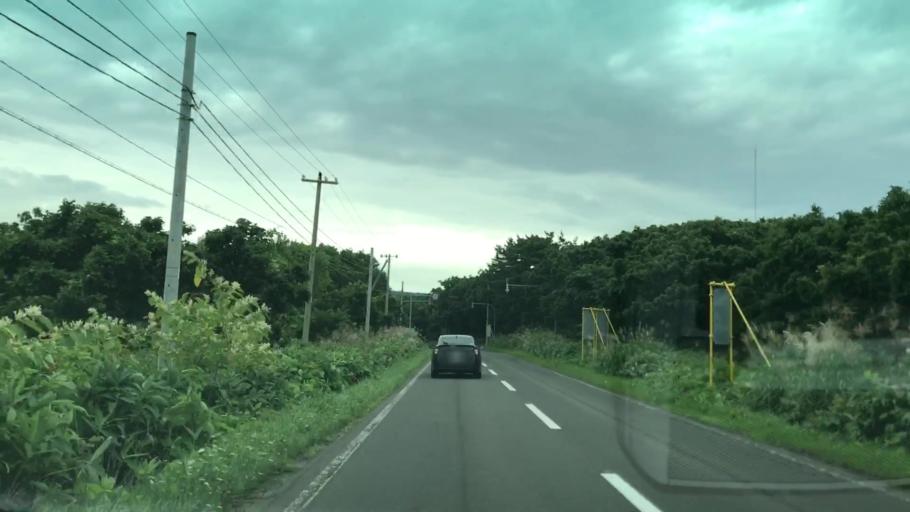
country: JP
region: Hokkaido
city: Iwanai
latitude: 42.8896
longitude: 140.3745
